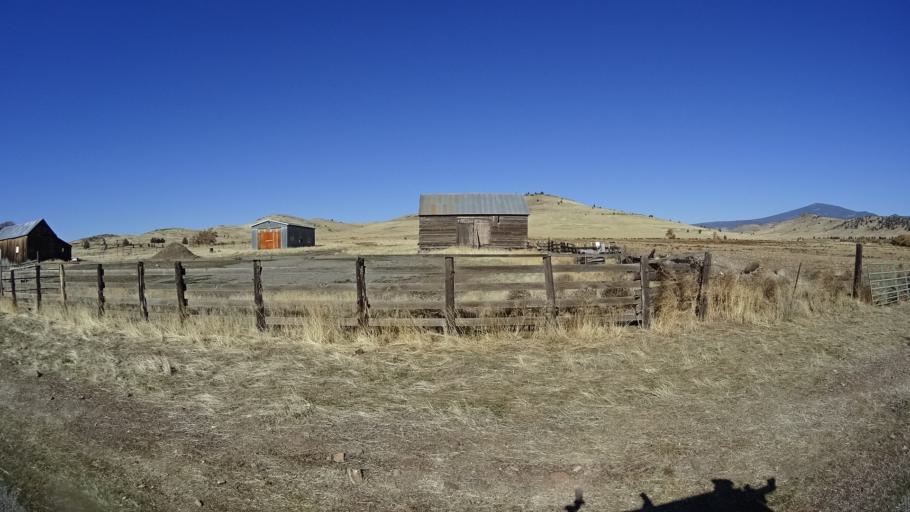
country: US
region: California
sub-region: Siskiyou County
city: Montague
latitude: 41.7263
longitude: -122.3802
